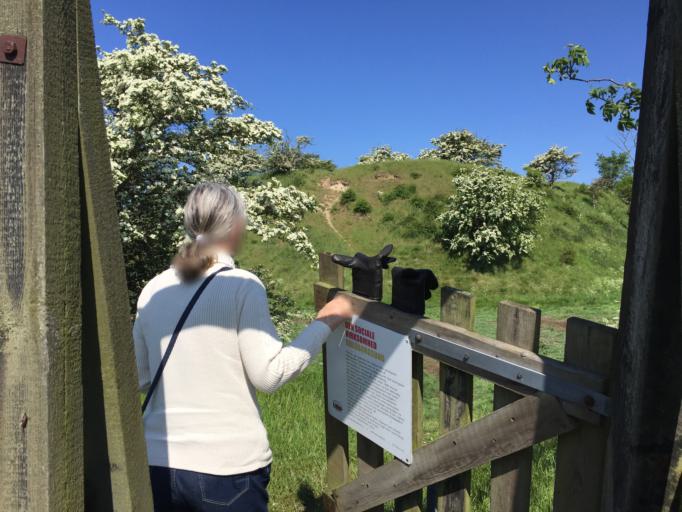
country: DK
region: Zealand
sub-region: Lolland Kommune
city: Maribo
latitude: 54.8955
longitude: 11.3624
